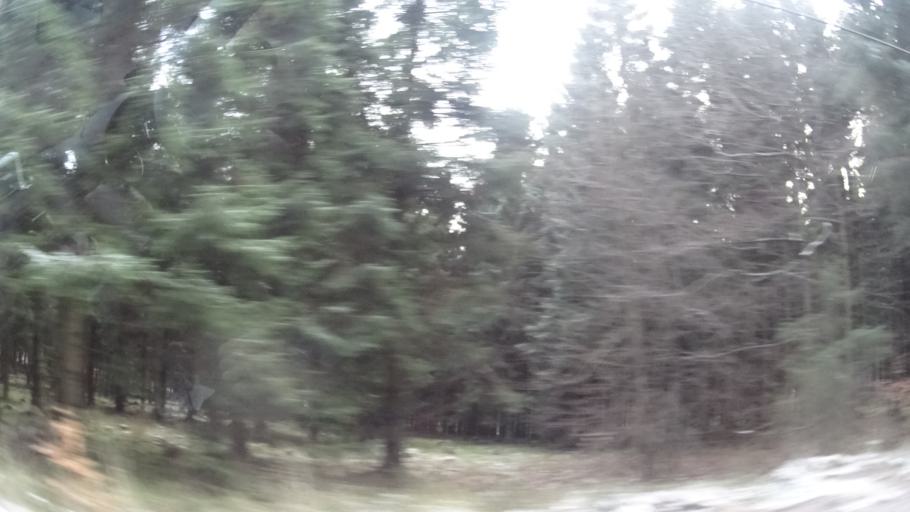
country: DE
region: Thuringia
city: Tabarz
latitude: 50.8392
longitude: 10.5190
